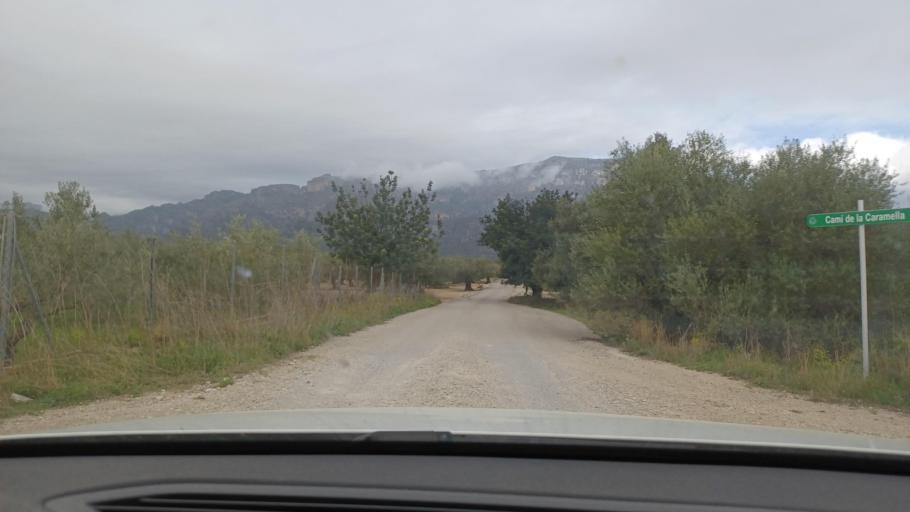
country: ES
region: Catalonia
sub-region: Provincia de Tarragona
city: Mas de Barberans
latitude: 40.7975
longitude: 0.4264
